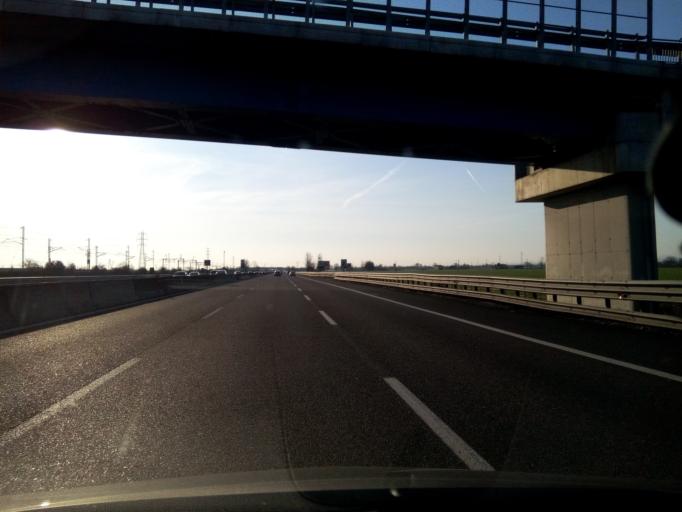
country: IT
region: Emilia-Romagna
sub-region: Provincia di Piacenza
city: Pontenure
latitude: 44.9964
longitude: 9.8240
